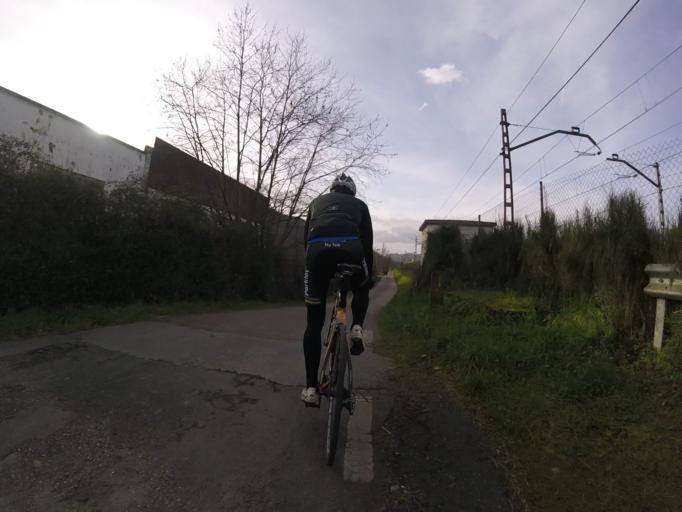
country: ES
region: Basque Country
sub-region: Provincia de Guipuzcoa
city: Villabona
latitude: 43.1802
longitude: -2.0577
